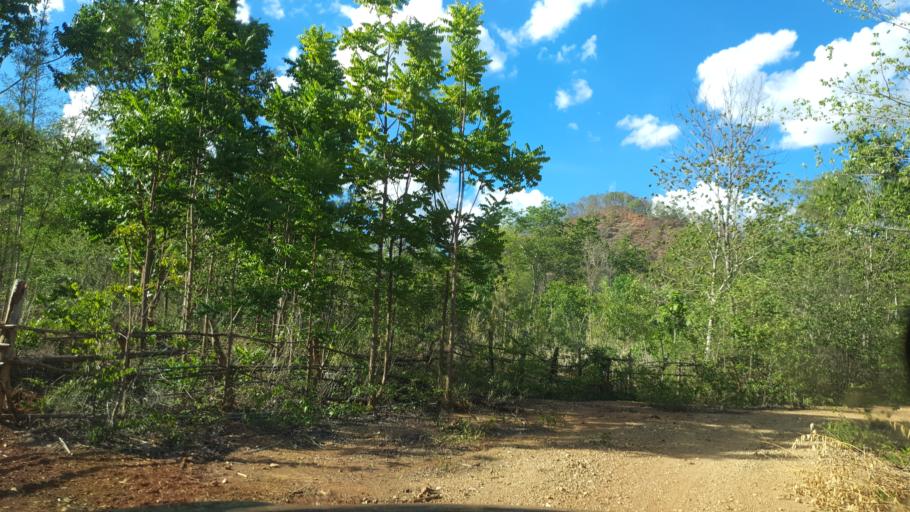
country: TH
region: Lampang
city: Sop Prap
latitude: 17.8404
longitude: 99.2858
